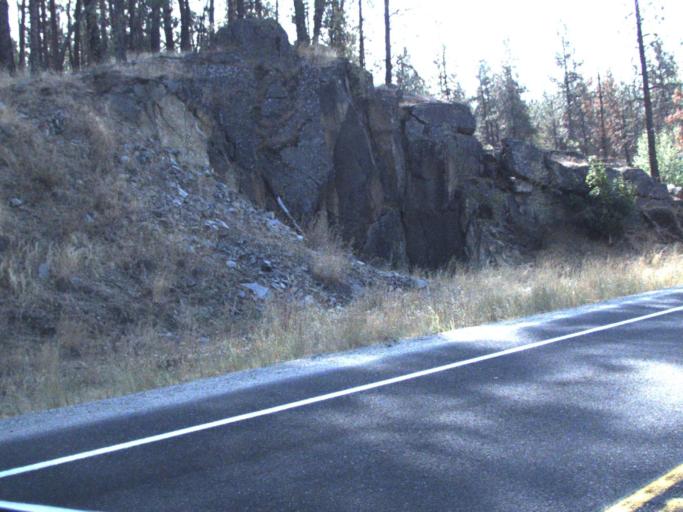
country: US
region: Washington
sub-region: Spokane County
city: Fairwood
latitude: 47.7729
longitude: -117.5426
